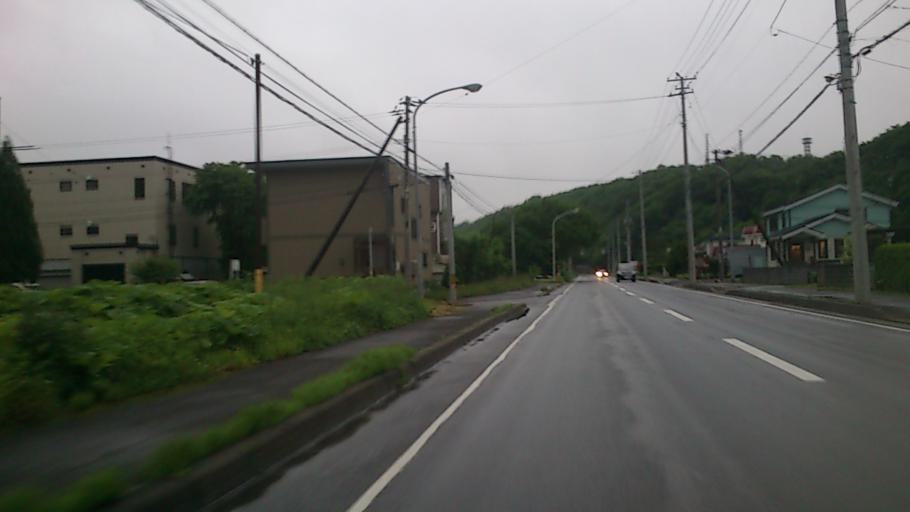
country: JP
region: Hokkaido
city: Chitose
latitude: 42.8173
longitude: 141.6162
